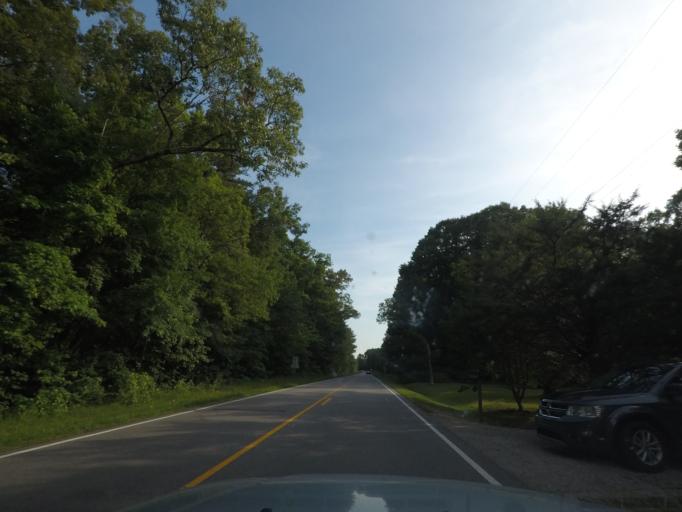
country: US
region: Virginia
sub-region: Mecklenburg County
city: Clarksville
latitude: 36.4865
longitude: -78.5486
